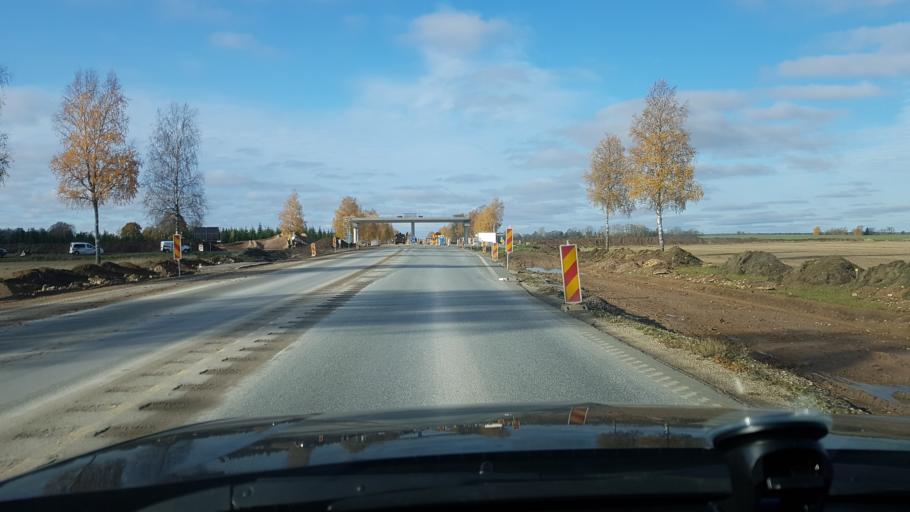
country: EE
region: Laeaene-Virumaa
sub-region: Haljala vald
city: Haljala
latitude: 59.4302
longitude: 26.2141
